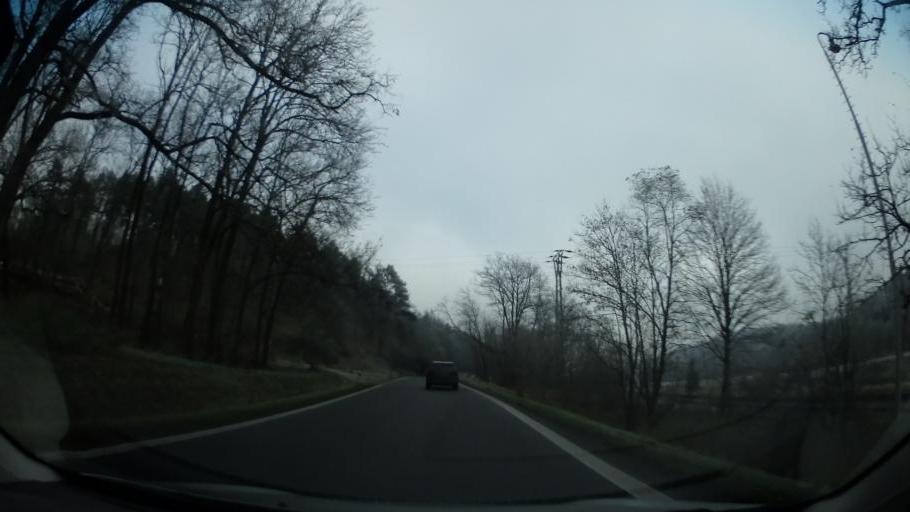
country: CZ
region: Vysocina
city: Vladislav
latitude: 49.2133
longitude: 15.9599
